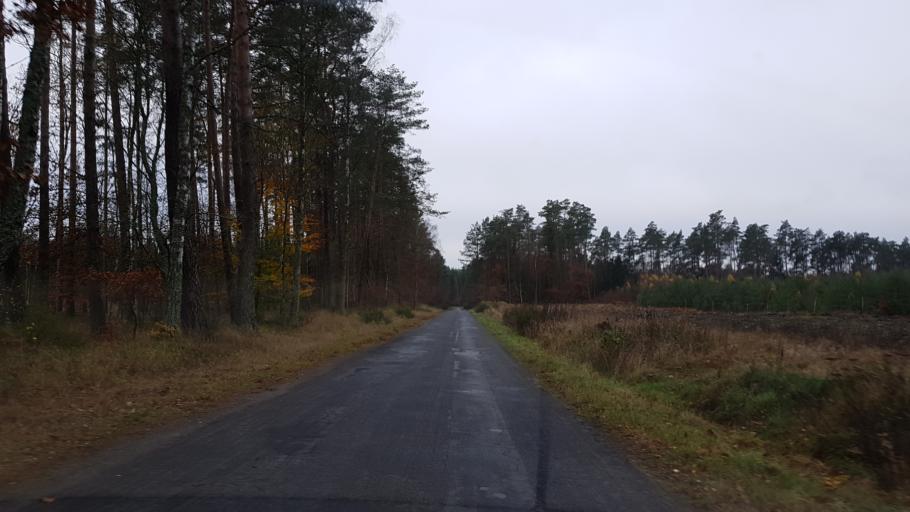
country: PL
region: West Pomeranian Voivodeship
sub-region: Powiat koszalinski
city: Bobolice
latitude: 54.0698
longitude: 16.5691
